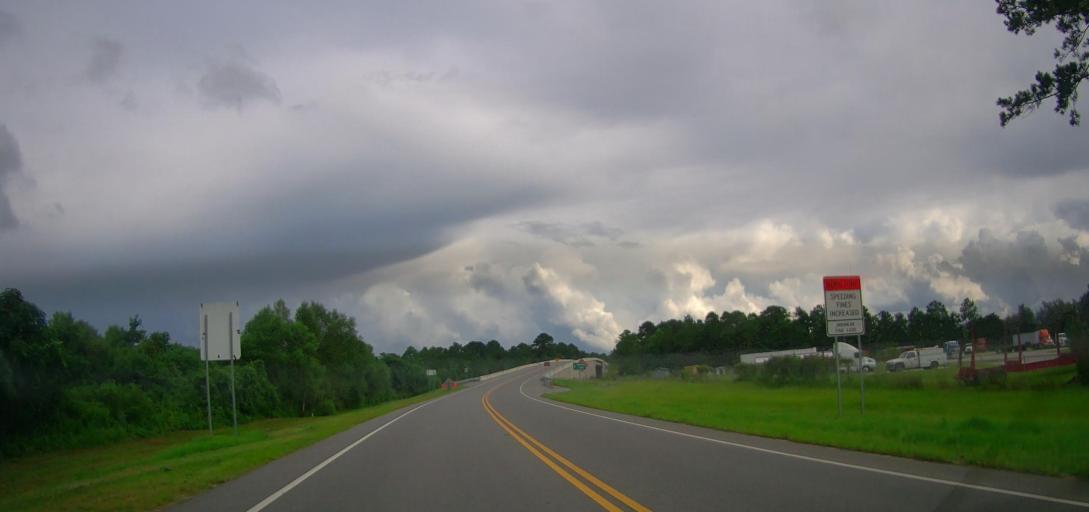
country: US
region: Georgia
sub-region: Wayne County
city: Jesup
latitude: 31.6220
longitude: -81.8959
